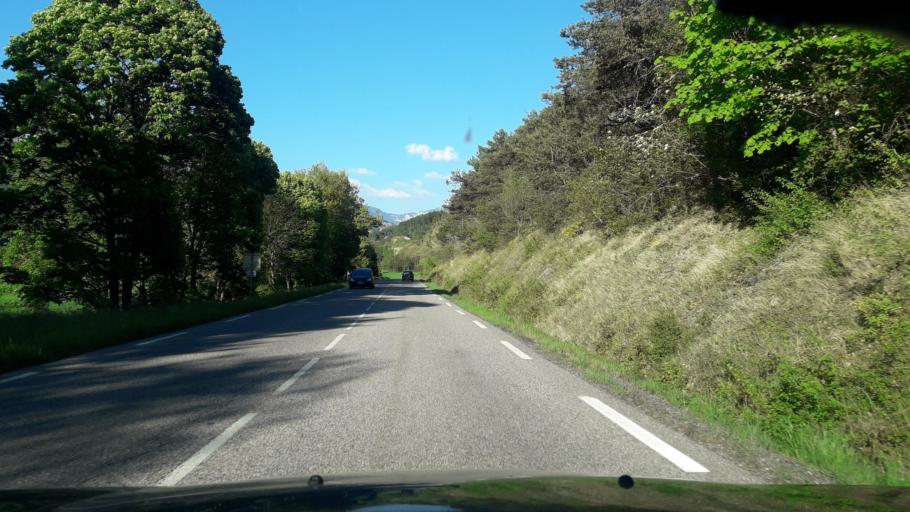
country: FR
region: Rhone-Alpes
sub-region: Departement de la Drome
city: Die
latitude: 44.7629
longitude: 5.3061
